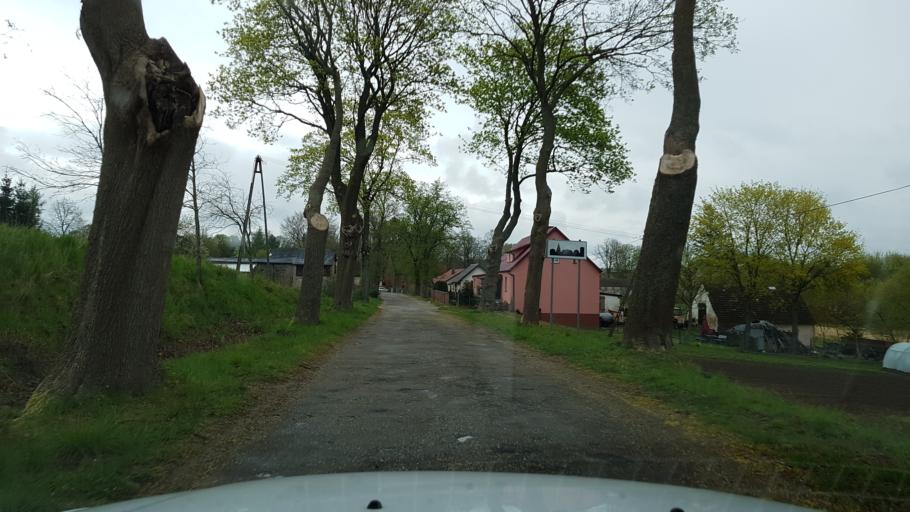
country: PL
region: West Pomeranian Voivodeship
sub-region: Powiat kolobrzeski
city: Ryman
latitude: 53.9658
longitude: 15.4523
